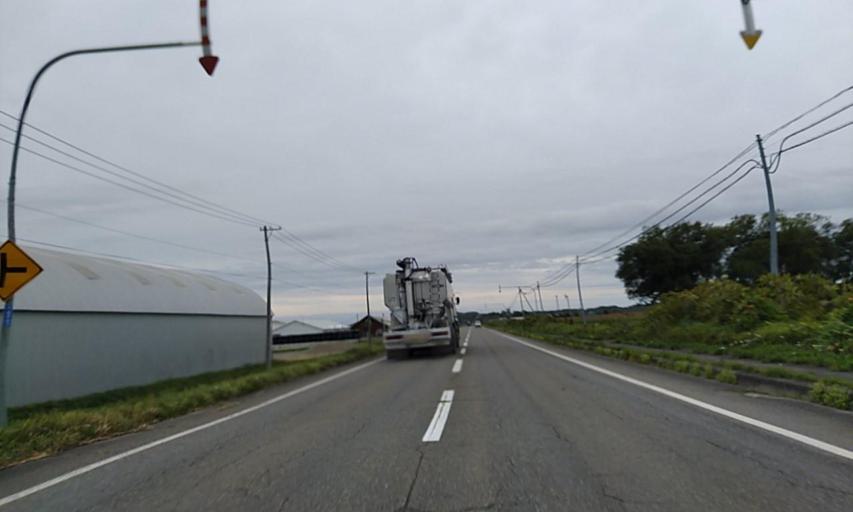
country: JP
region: Hokkaido
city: Obihiro
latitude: 42.4613
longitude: 143.2802
